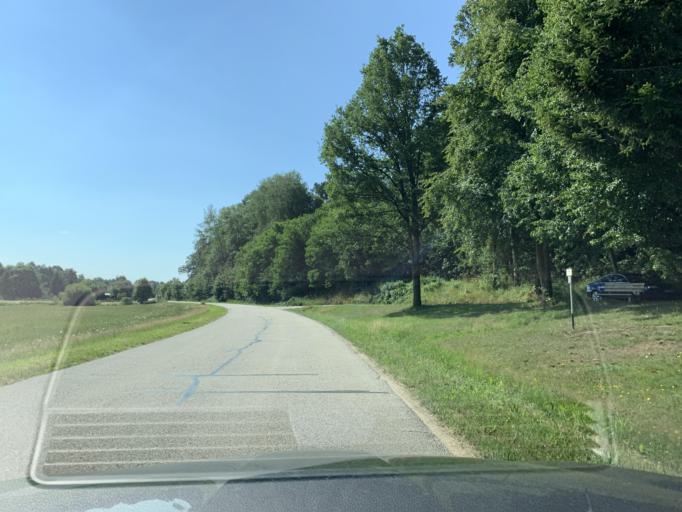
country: DE
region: Bavaria
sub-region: Upper Palatinate
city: Schwarzhofen
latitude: 49.3708
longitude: 12.3424
